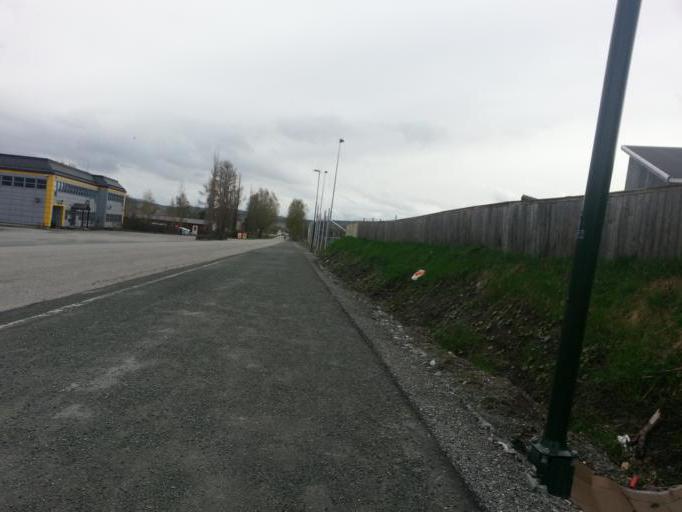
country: NO
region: Nord-Trondelag
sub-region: Levanger
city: Skogn
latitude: 63.7020
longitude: 11.1946
